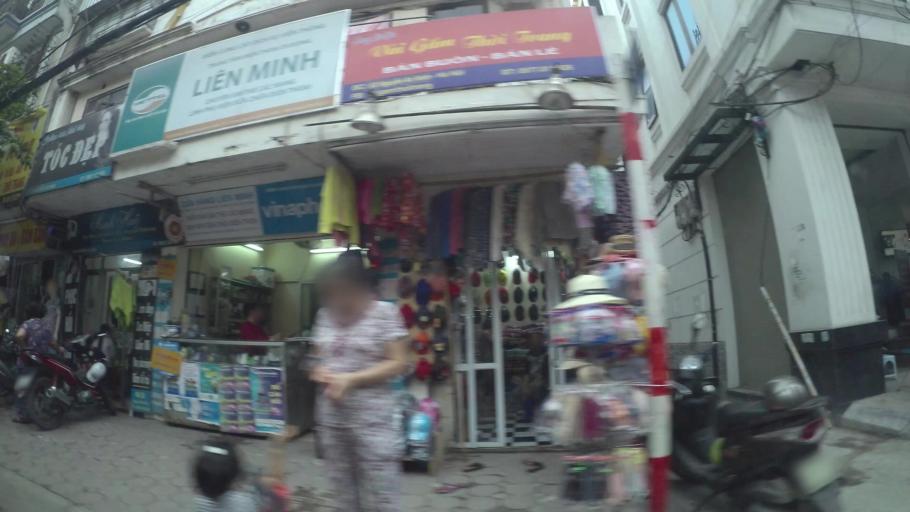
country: VN
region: Ha Noi
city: Hai BaTrung
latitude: 20.9905
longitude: 105.8450
